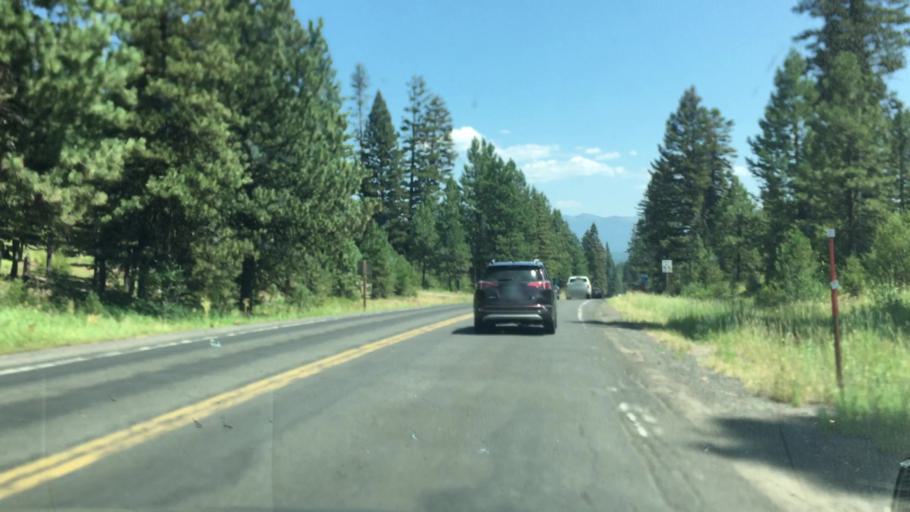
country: US
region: Idaho
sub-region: Valley County
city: McCall
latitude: 44.9290
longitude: -116.1517
